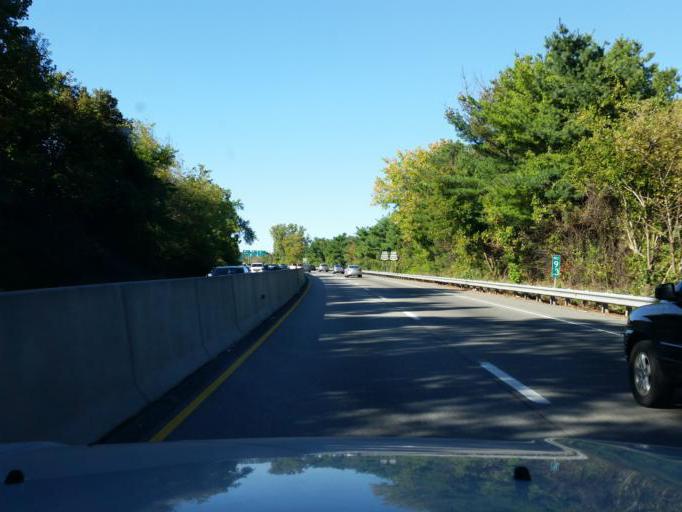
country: US
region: Pennsylvania
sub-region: Chester County
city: West Chester
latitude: 39.9614
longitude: -75.5798
